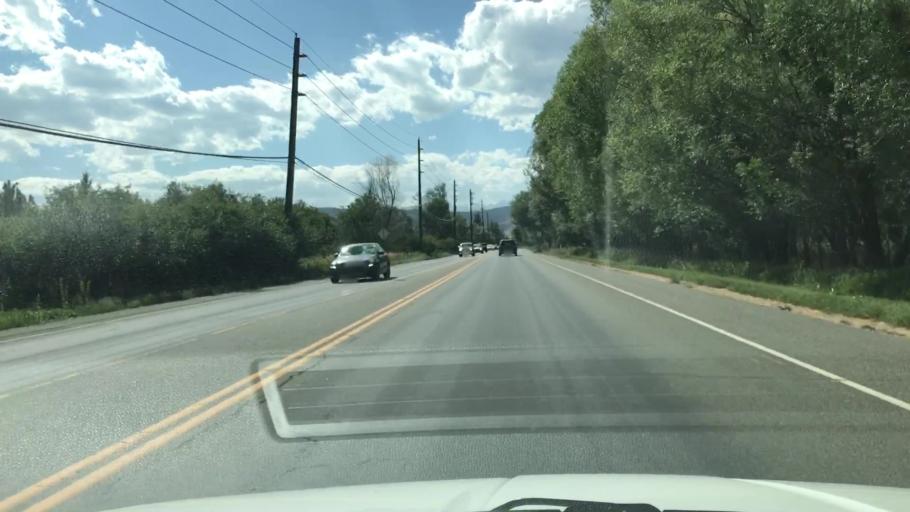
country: US
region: Colorado
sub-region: Boulder County
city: Gunbarrel
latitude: 40.0511
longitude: -105.2176
